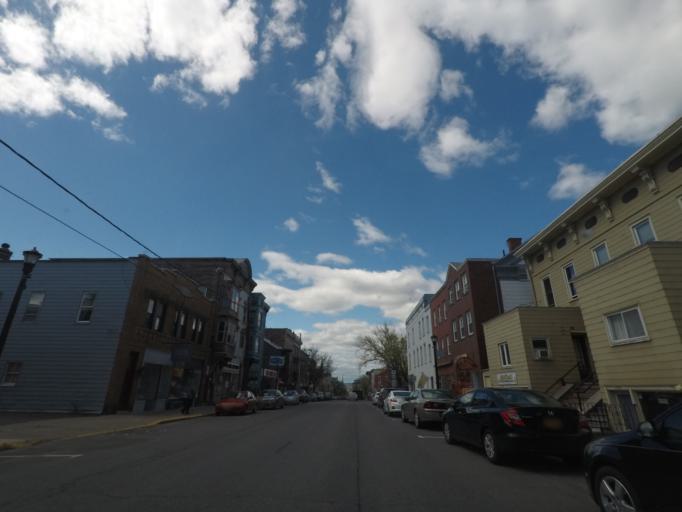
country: US
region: New York
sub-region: Columbia County
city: Oakdale
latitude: 42.2466
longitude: -73.7825
